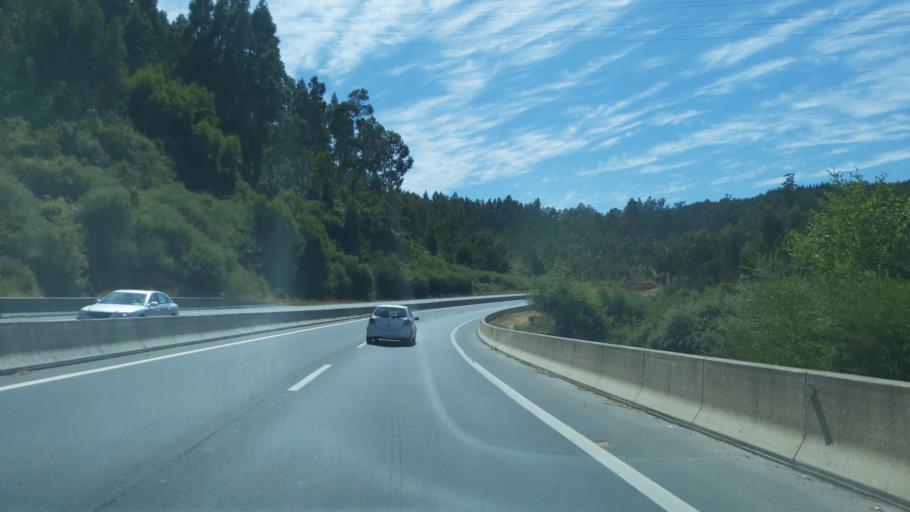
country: CL
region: Biobio
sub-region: Provincia de Concepcion
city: Lota
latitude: -37.0720
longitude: -73.1399
